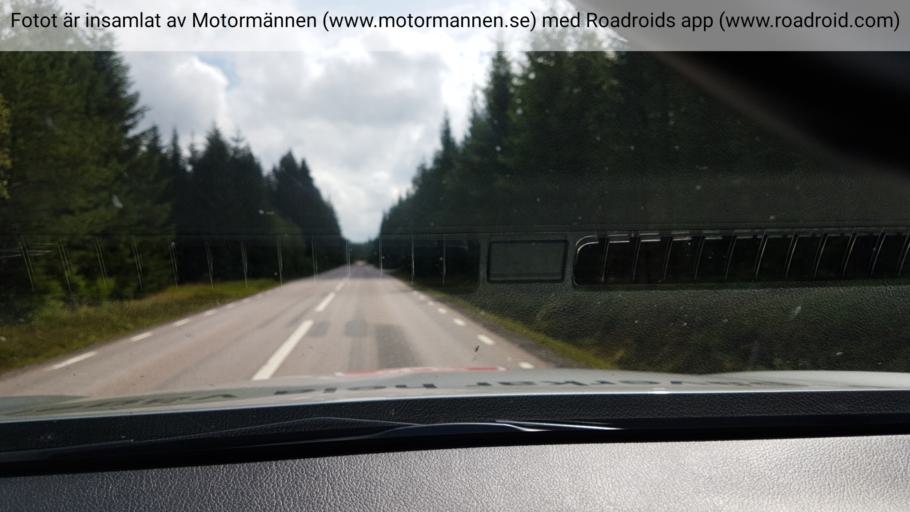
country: SE
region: Vaestra Goetaland
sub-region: Marks Kommun
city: Fritsla
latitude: 57.4951
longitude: 12.9409
